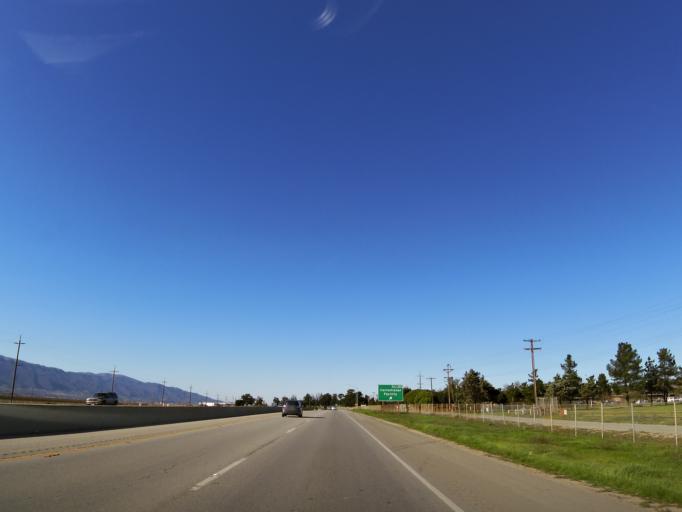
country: US
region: California
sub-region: Monterey County
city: Soledad
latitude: 36.4614
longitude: -121.3823
